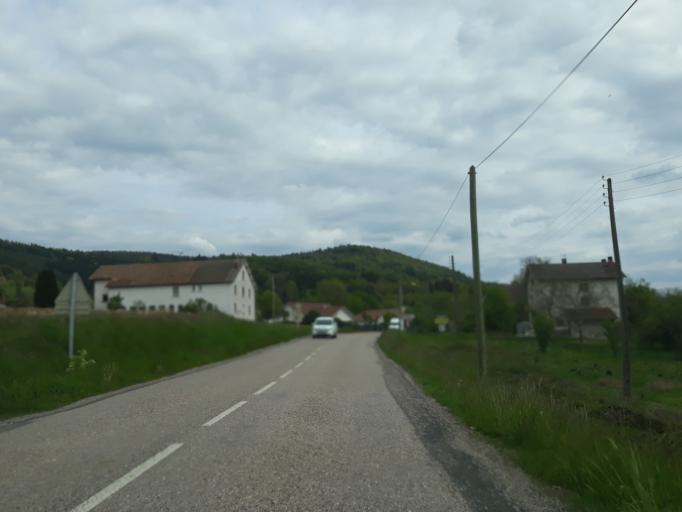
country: FR
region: Lorraine
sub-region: Departement des Vosges
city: Granges-sur-Vologne
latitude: 48.1713
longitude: 6.7736
